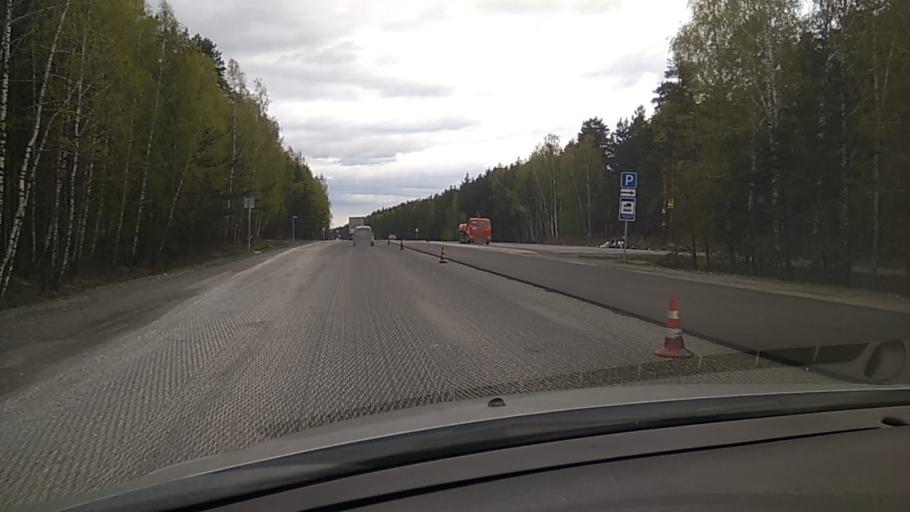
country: RU
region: Sverdlovsk
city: Verkhneye Dubrovo
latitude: 56.6904
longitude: 61.1064
